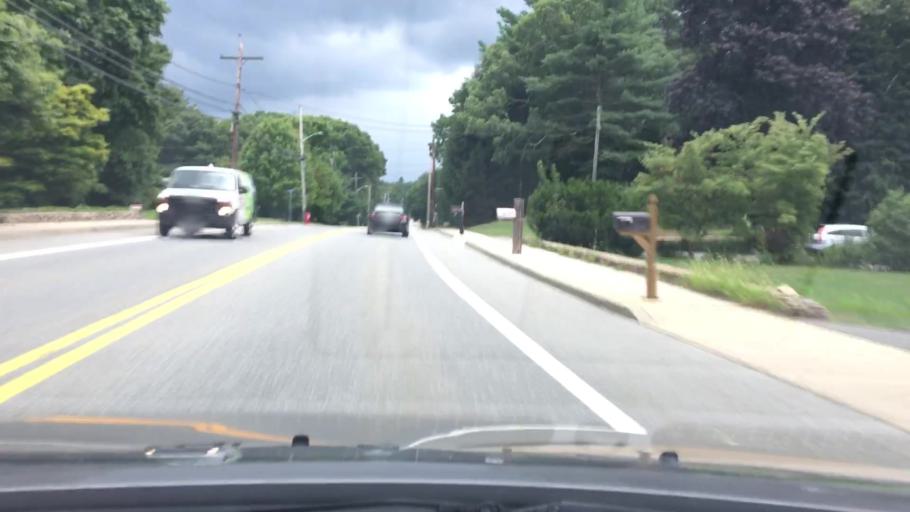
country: US
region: Rhode Island
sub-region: Providence County
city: Cumberland
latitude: 41.9782
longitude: -71.3918
